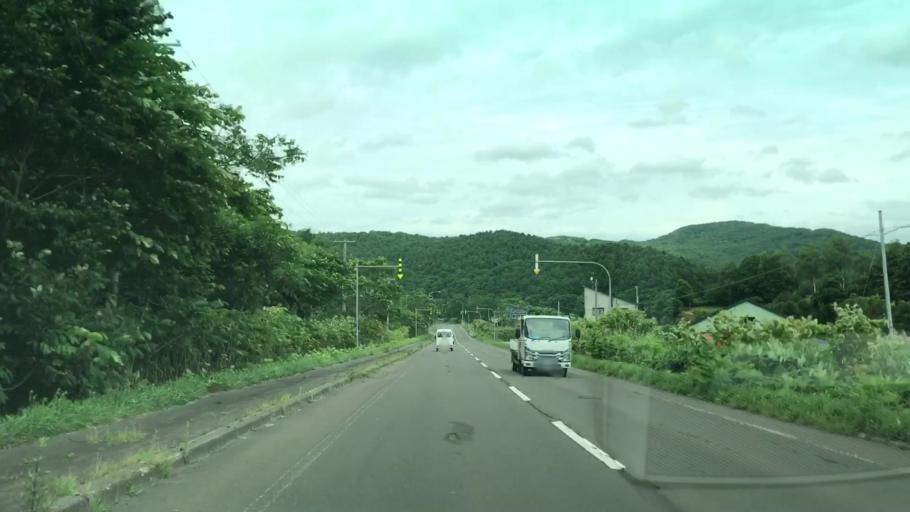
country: JP
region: Hokkaido
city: Niseko Town
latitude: 42.9607
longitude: 140.6937
